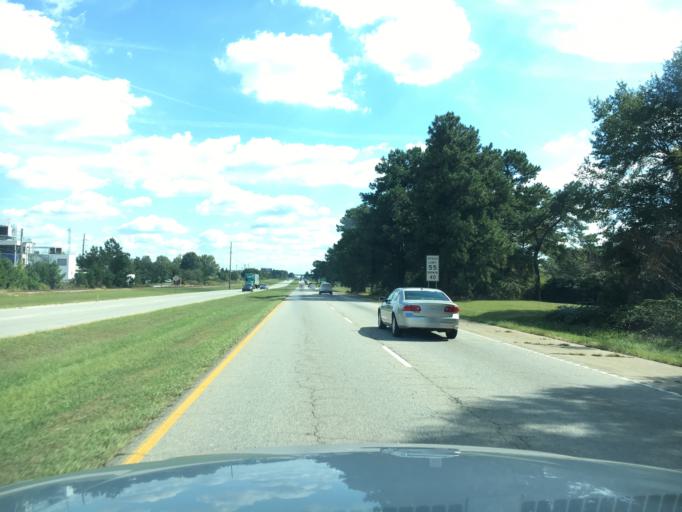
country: US
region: South Carolina
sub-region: Greenville County
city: Mauldin
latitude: 34.7709
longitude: -82.3008
